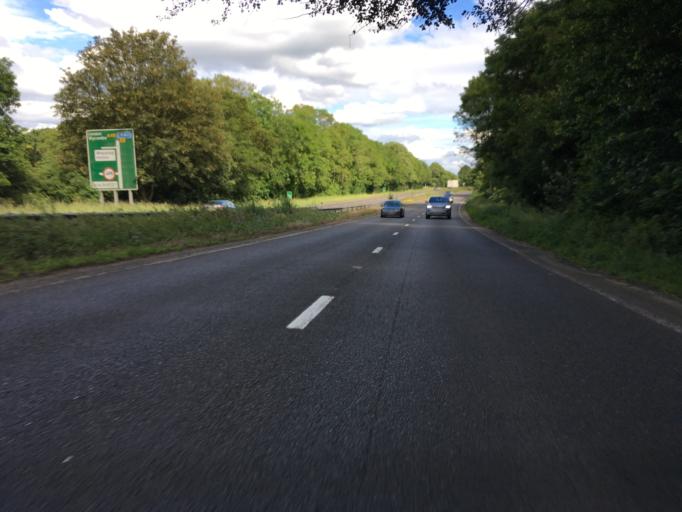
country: GB
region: England
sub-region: Oxfordshire
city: Wheatley
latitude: 51.7572
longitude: -1.1478
